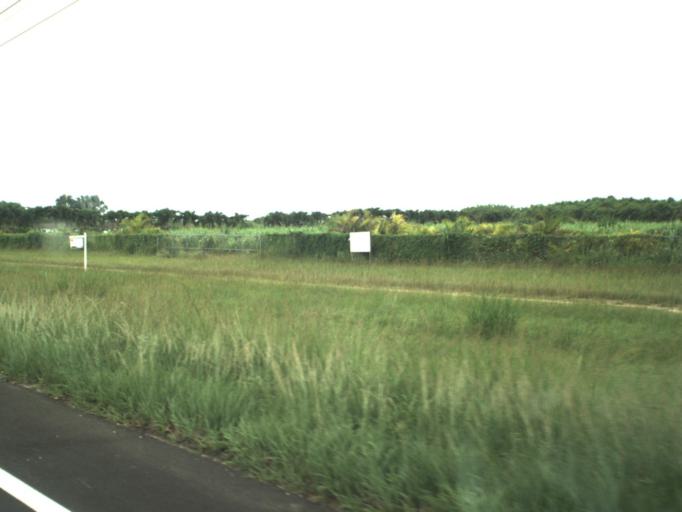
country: US
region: Florida
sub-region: Miami-Dade County
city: Country Walk
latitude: 25.6261
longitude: -80.4796
